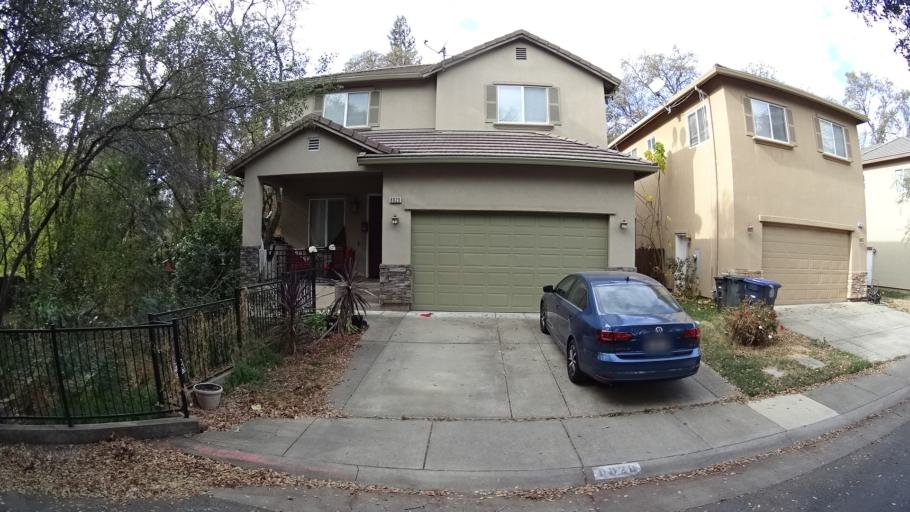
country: US
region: California
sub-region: Sacramento County
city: Fair Oaks
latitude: 38.6684
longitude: -121.2661
